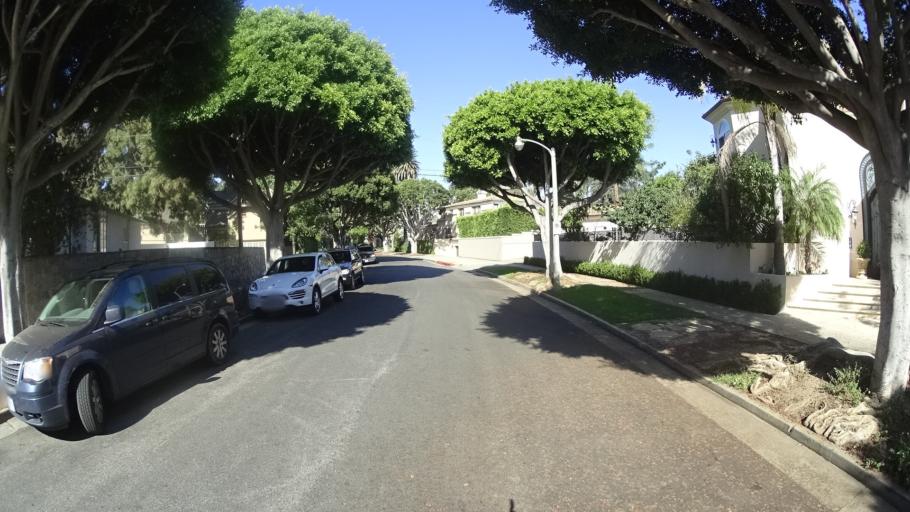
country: US
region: California
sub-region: Los Angeles County
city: Santa Monica
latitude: 34.0448
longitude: -118.4947
